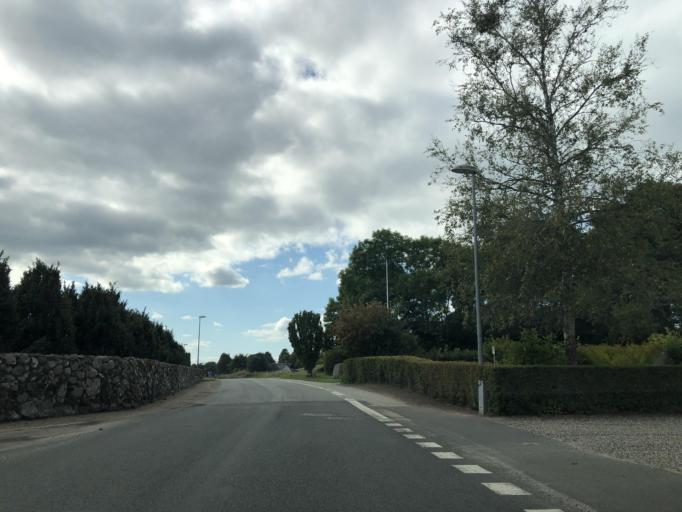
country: DK
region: Central Jutland
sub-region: Viborg Kommune
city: Viborg
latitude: 56.5789
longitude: 9.3825
